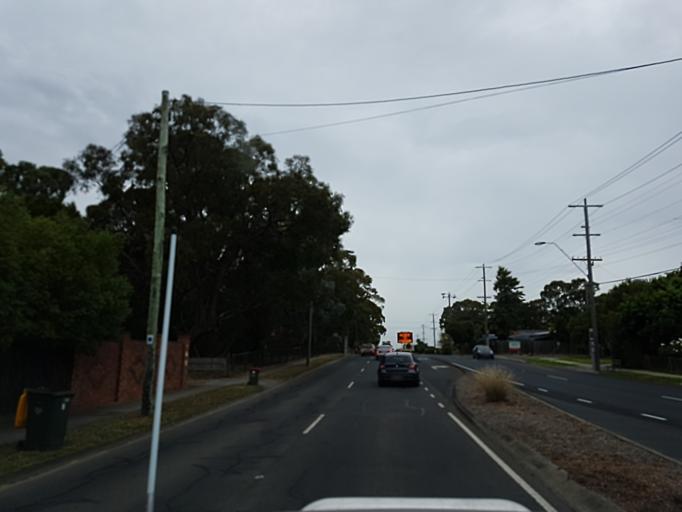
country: AU
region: Victoria
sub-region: Whitehorse
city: Blackburn South
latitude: -37.8321
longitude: 145.1516
